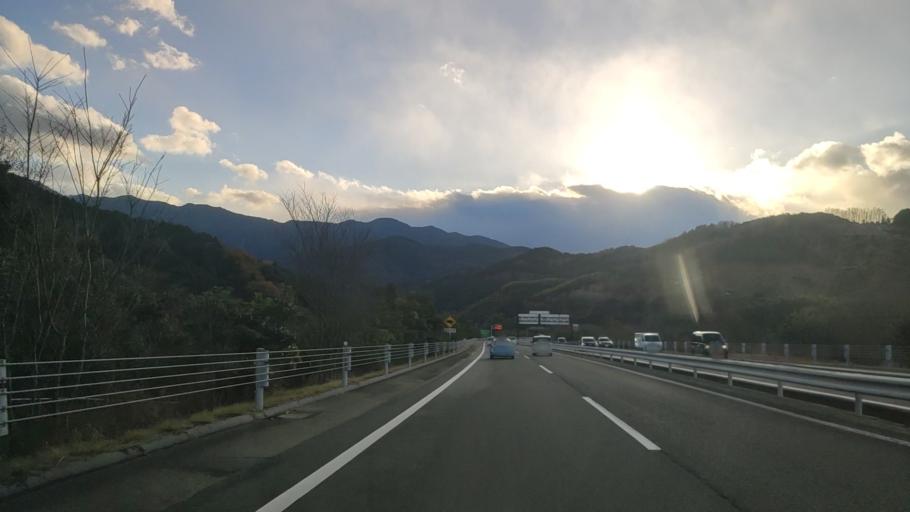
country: JP
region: Ehime
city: Saijo
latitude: 33.8797
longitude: 133.0842
